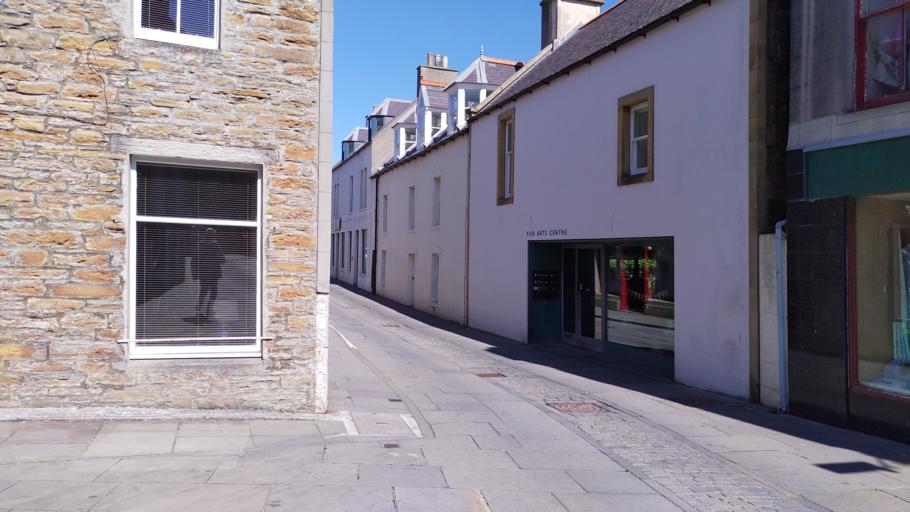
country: GB
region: Scotland
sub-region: Orkney Islands
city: Stromness
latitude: 58.9629
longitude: -3.2986
